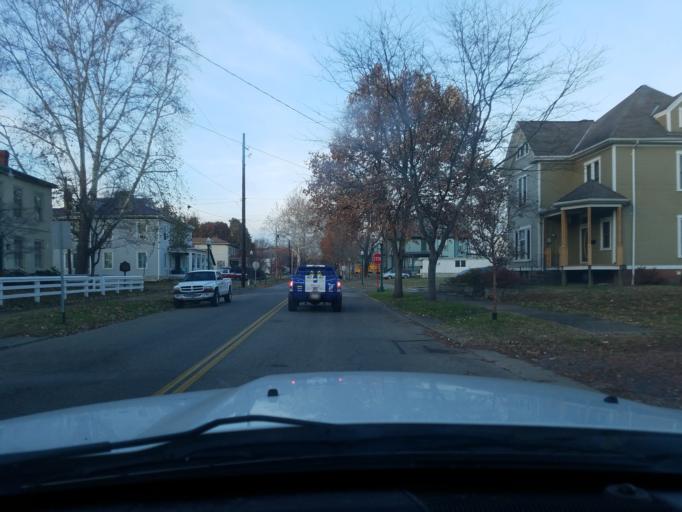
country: US
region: Ohio
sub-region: Washington County
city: Marietta
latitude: 39.4091
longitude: -81.4598
